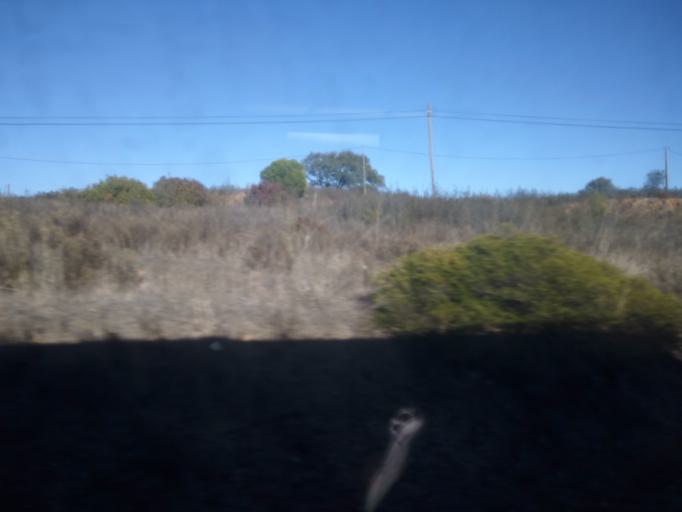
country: PT
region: Faro
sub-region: Silves
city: Sao Bartolomeu de Messines
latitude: 37.3160
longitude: -8.3246
